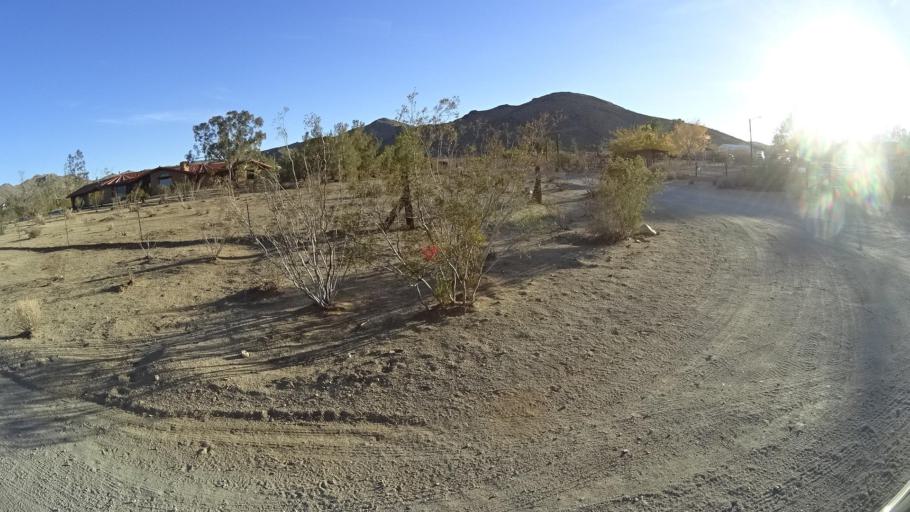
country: US
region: California
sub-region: Kern County
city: Ridgecrest
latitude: 35.5825
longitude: -117.6567
